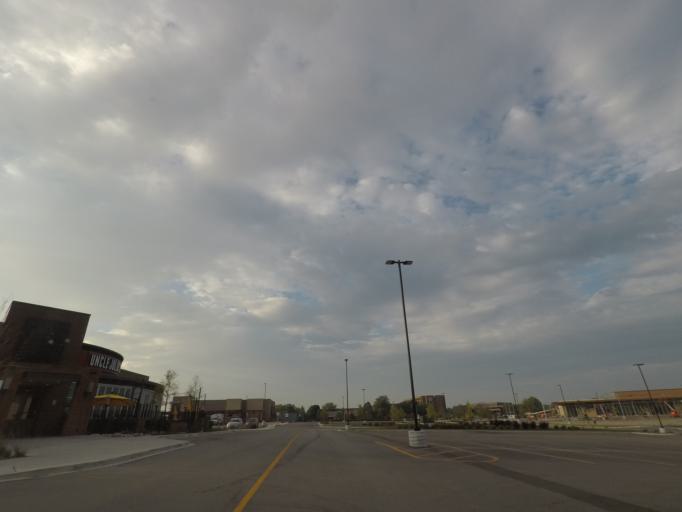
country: US
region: Wisconsin
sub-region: Waukesha County
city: Brookfield
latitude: 43.0301
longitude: -88.1077
